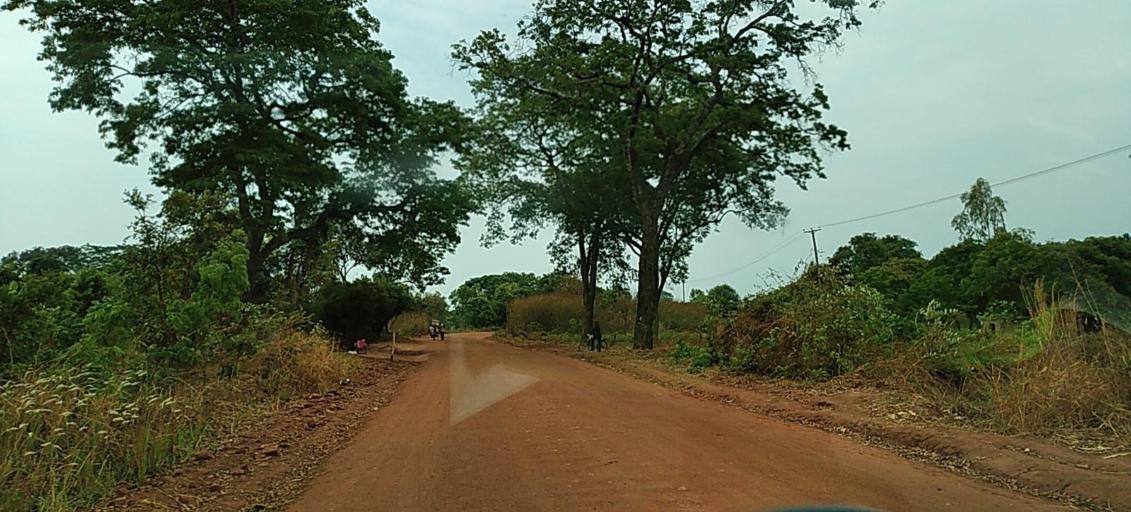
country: ZM
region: North-Western
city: Solwezi
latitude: -12.2396
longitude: 26.5116
